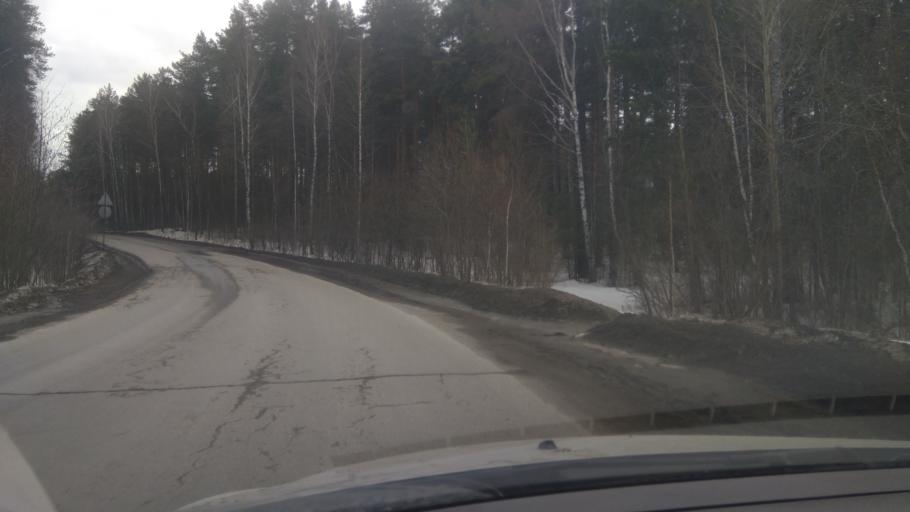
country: RU
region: Sverdlovsk
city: Severka
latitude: 56.8352
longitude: 60.3824
